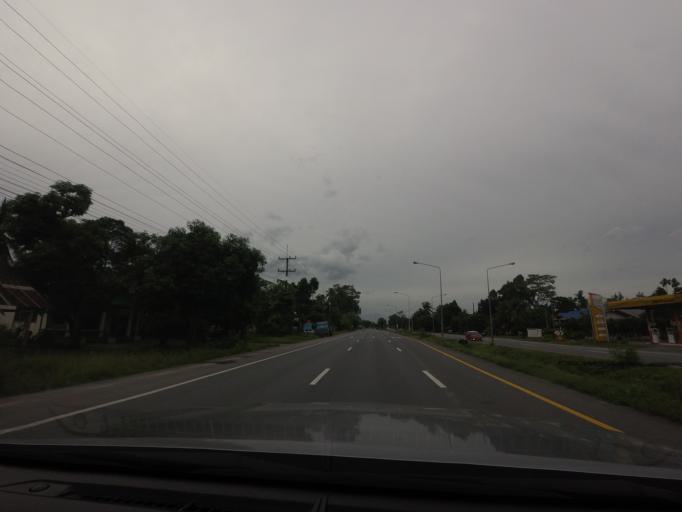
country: TH
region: Nakhon Si Thammarat
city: Chaloem Phra Kiat
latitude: 8.1582
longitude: 100.0555
